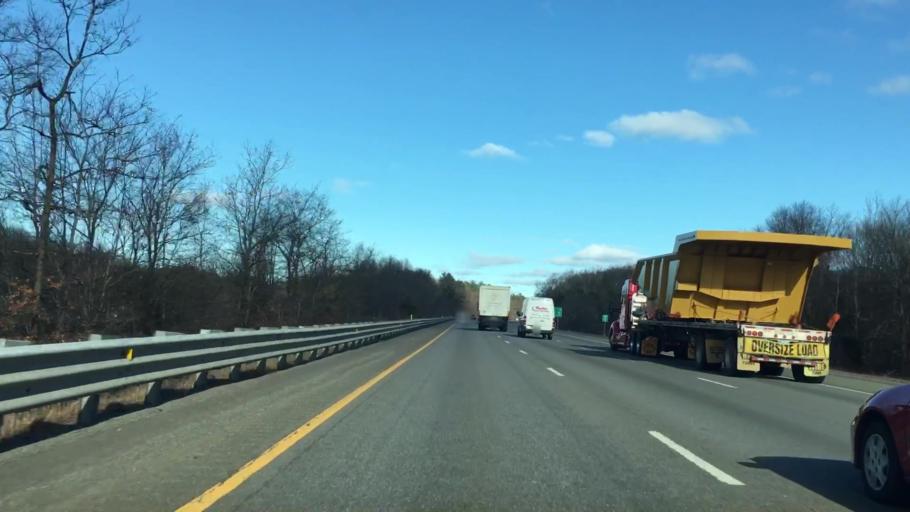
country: US
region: Massachusetts
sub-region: Worcester County
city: Bolton
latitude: 42.4018
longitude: -71.6077
